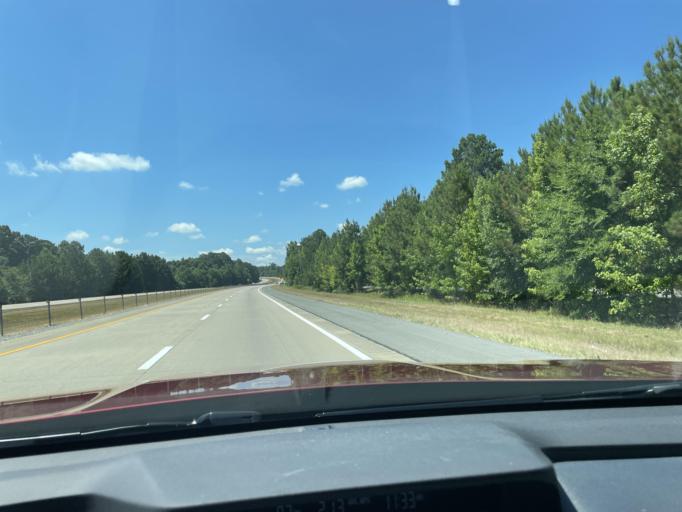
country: US
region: Arkansas
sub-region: Jefferson County
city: Redfield
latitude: 34.4791
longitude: -92.2083
